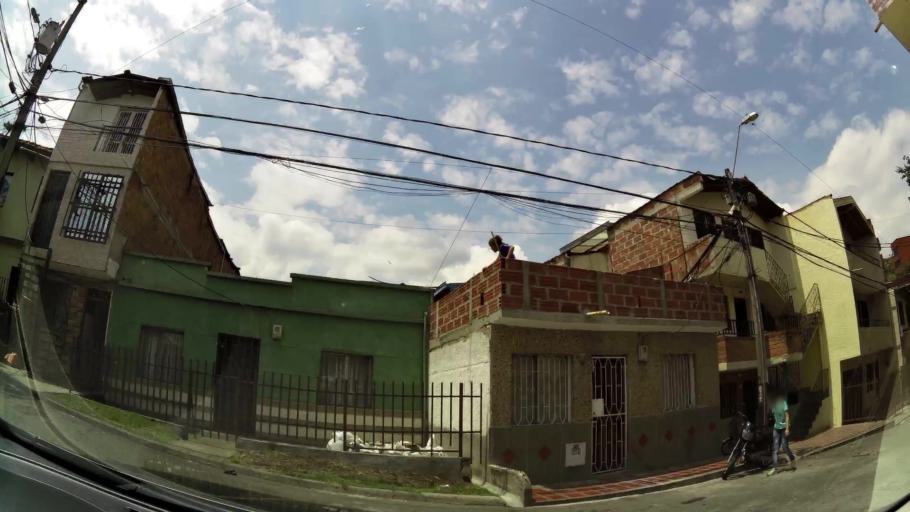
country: CO
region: Antioquia
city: Medellin
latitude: 6.2538
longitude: -75.6183
